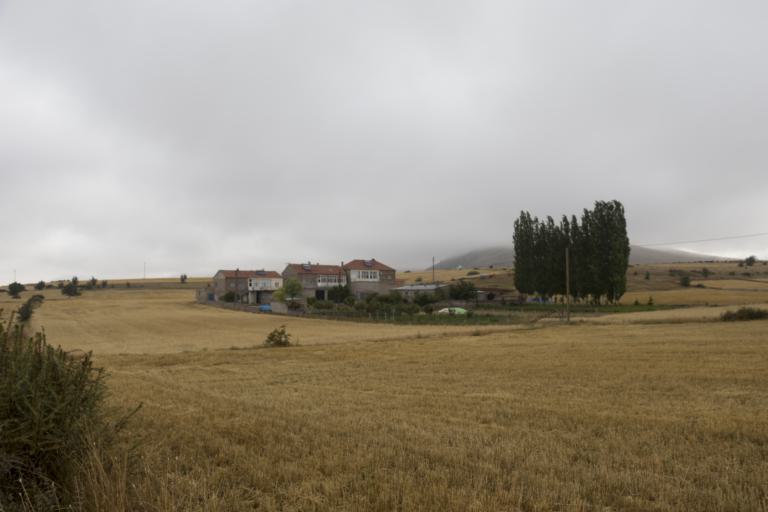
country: TR
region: Kayseri
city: Toklar
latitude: 38.4094
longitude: 36.0842
